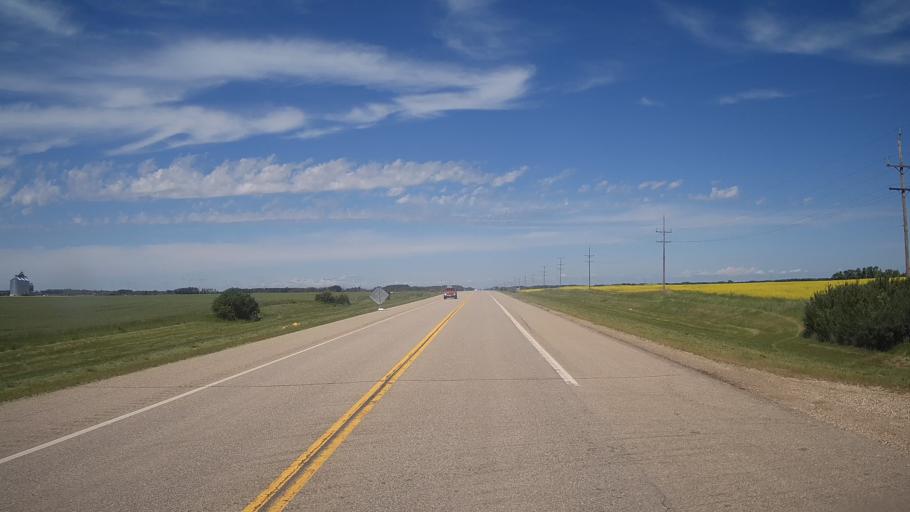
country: CA
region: Saskatchewan
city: Langenburg
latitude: 50.6326
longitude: -101.2760
